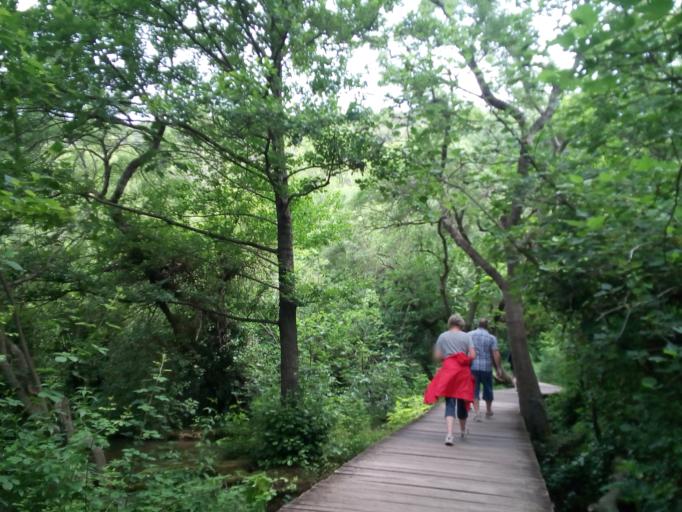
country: HR
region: Sibensko-Kniniska
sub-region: Grad Sibenik
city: Sibenik
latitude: 43.8049
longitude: 15.9669
